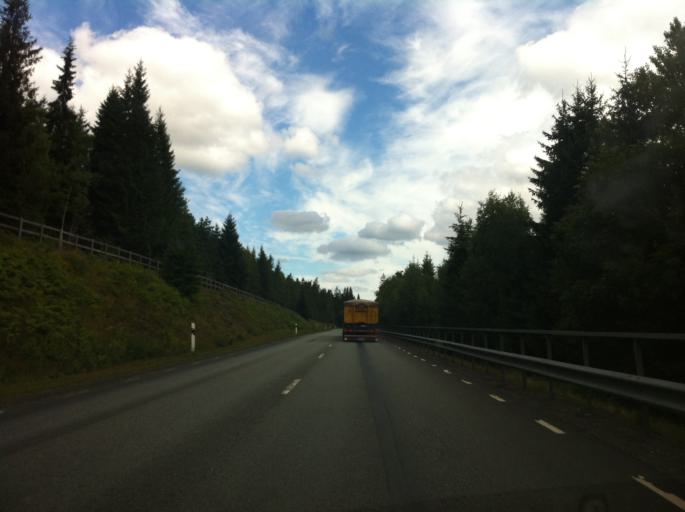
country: SE
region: Joenkoeping
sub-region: Gislaveds Kommun
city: Gislaved
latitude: 57.3751
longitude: 13.5777
